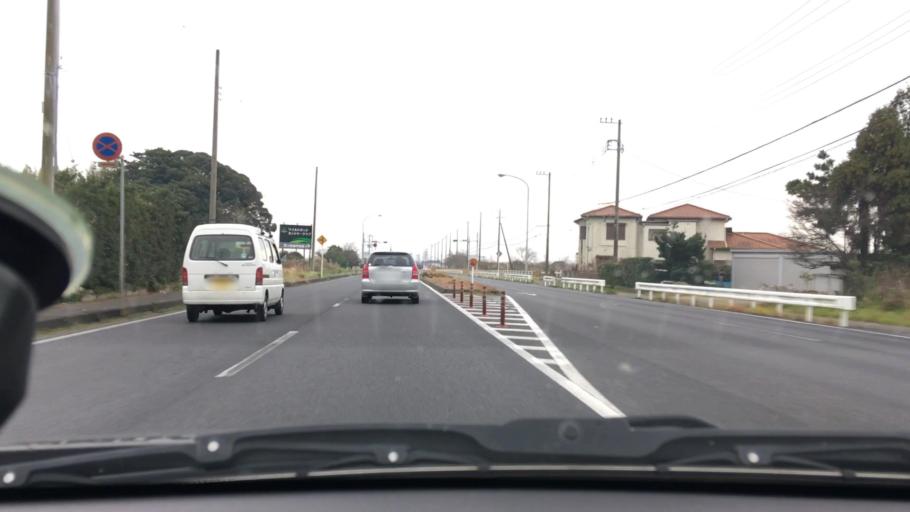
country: JP
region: Ibaraki
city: Kashima-shi
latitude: 35.9169
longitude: 140.6188
